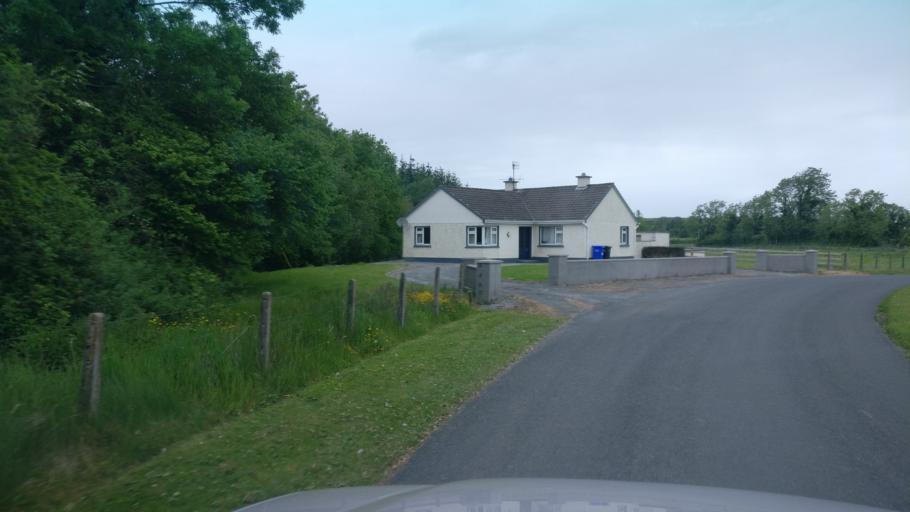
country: IE
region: Connaught
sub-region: County Galway
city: Loughrea
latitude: 53.1170
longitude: -8.4251
